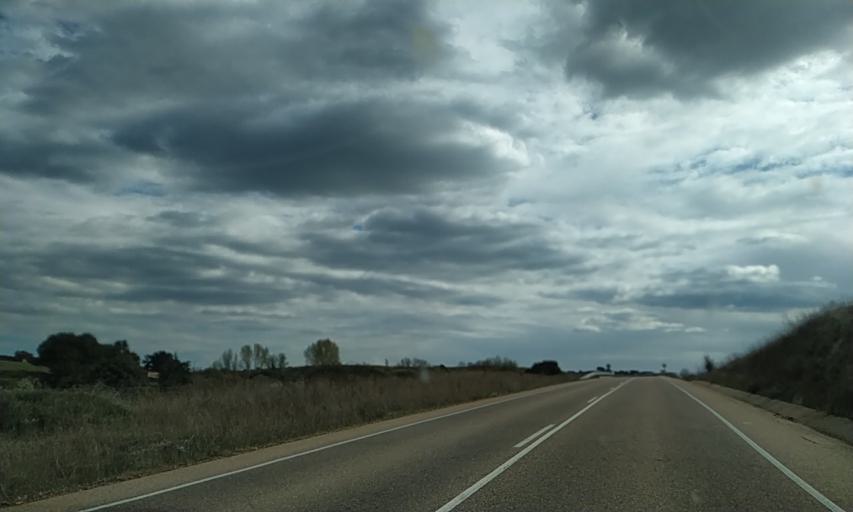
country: ES
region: Castille and Leon
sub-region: Provincia de Salamanca
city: Herguijuela de Ciudad Rodrigo
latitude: 40.4894
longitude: -6.5815
